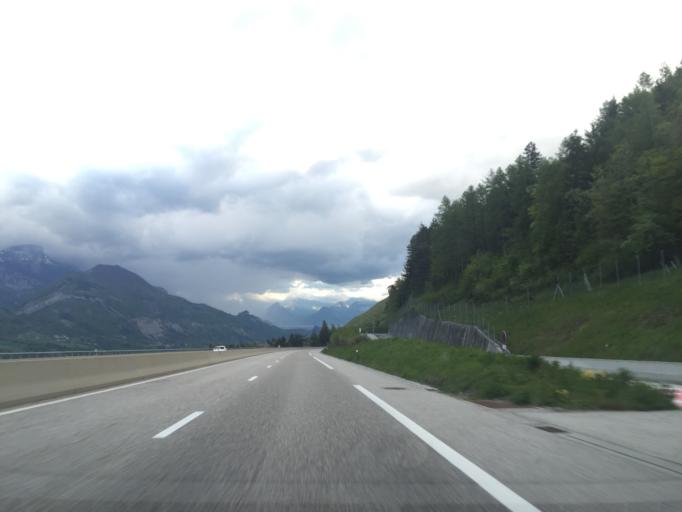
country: FR
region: Rhone-Alpes
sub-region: Departement de l'Isere
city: Le Gua
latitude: 44.9859
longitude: 5.6487
